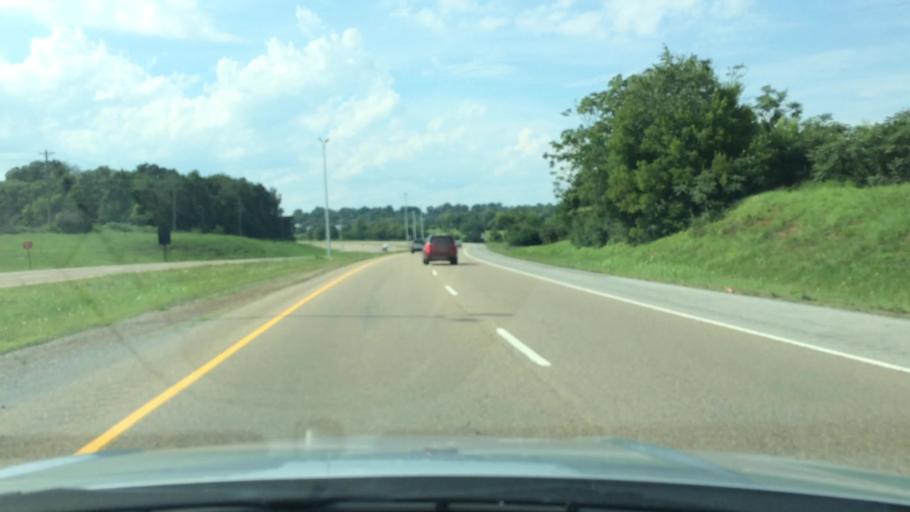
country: US
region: Tennessee
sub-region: Hamblen County
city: Morristown
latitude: 36.1730
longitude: -83.3876
